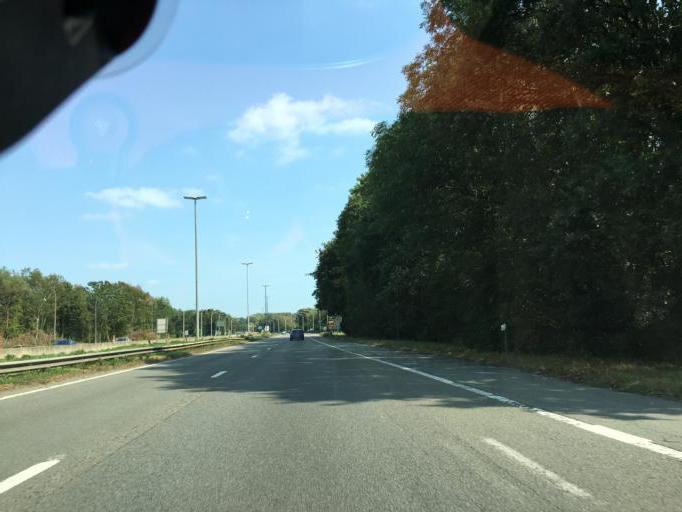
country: BE
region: Wallonia
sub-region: Province du Hainaut
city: Manage
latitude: 50.4985
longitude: 4.2113
